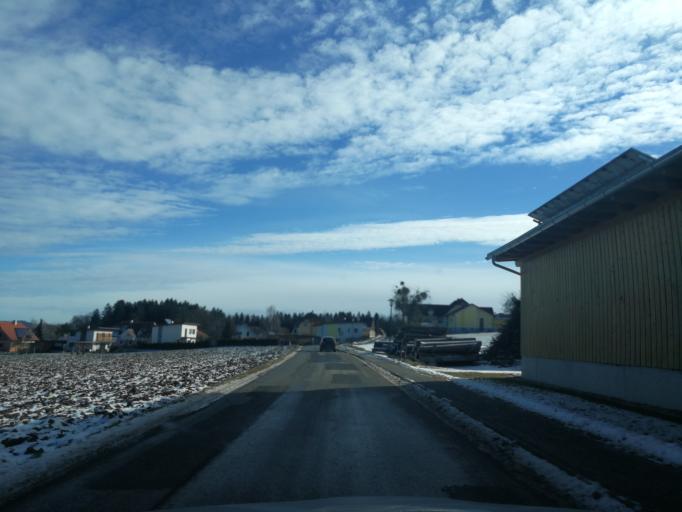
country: AT
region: Styria
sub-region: Politischer Bezirk Weiz
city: Ungerdorf
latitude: 47.0996
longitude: 15.6557
